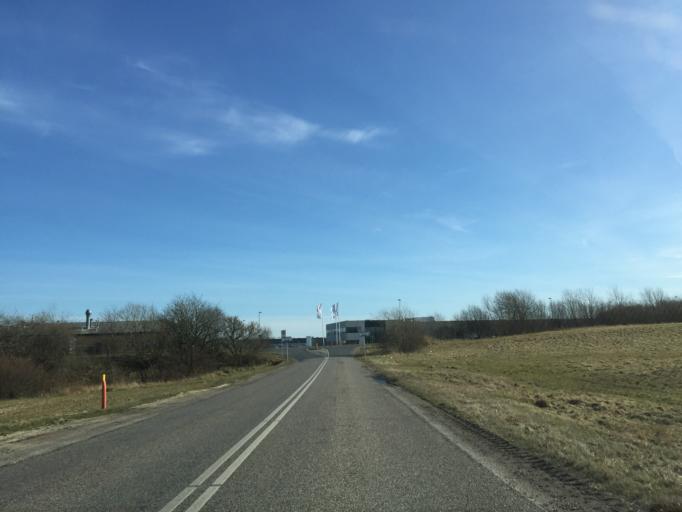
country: DK
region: Central Jutland
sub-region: Silkeborg Kommune
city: Silkeborg
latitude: 56.2062
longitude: 9.5647
